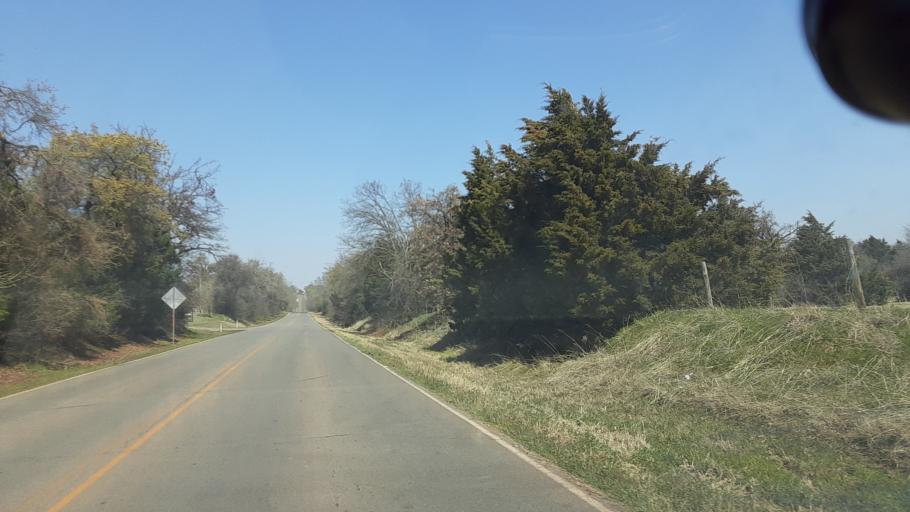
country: US
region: Oklahoma
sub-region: Oklahoma County
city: Edmond
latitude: 35.7660
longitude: -97.4784
